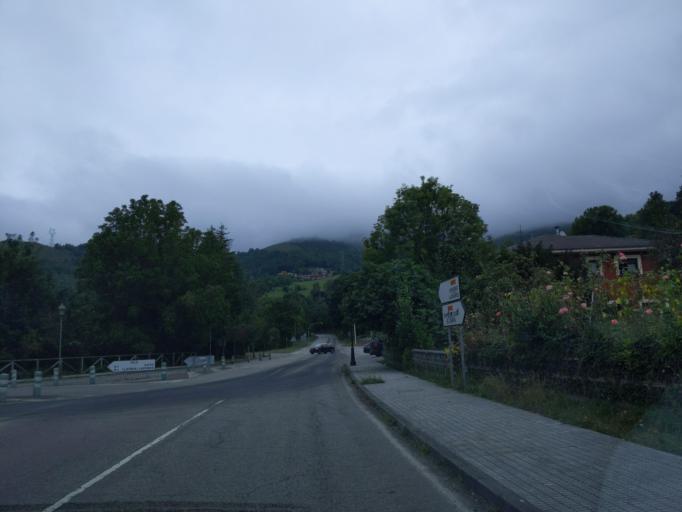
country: ES
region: Asturias
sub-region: Province of Asturias
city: Pola de Laviana
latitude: 43.2221
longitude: -5.4578
